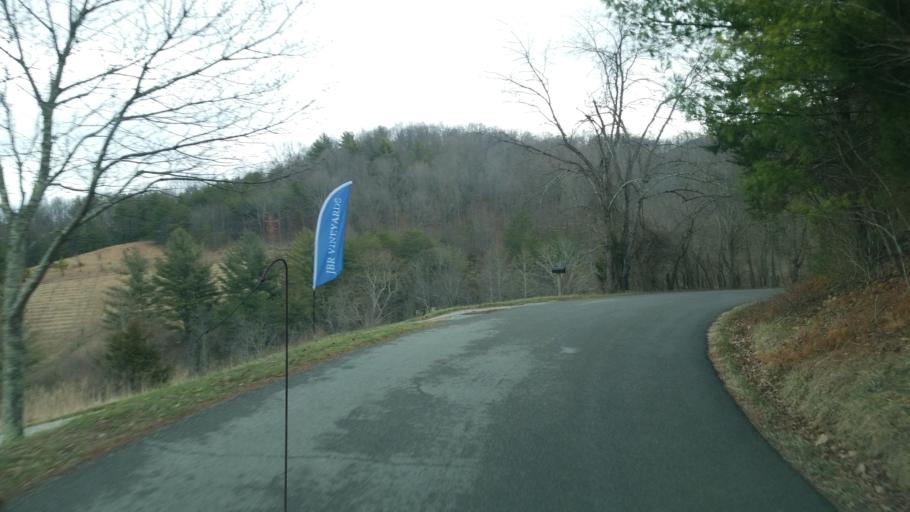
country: US
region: Virginia
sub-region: Giles County
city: Pearisburg
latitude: 37.2244
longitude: -80.6984
